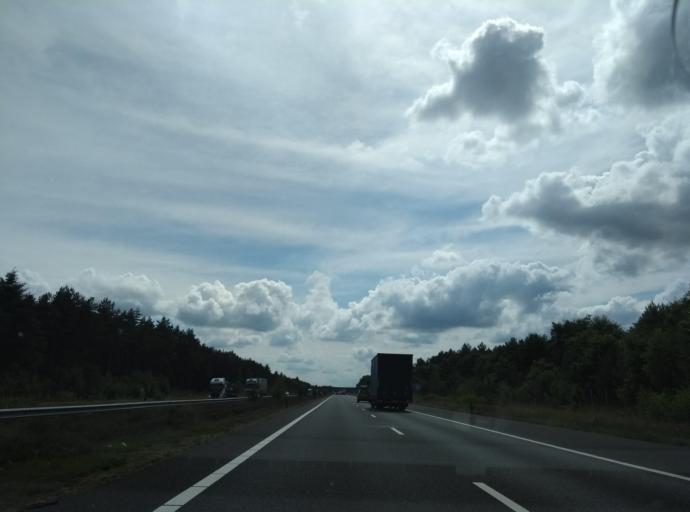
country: NL
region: North Brabant
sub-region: Gemeente Bladel en Netersel
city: Bladel
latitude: 51.3348
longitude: 5.2486
